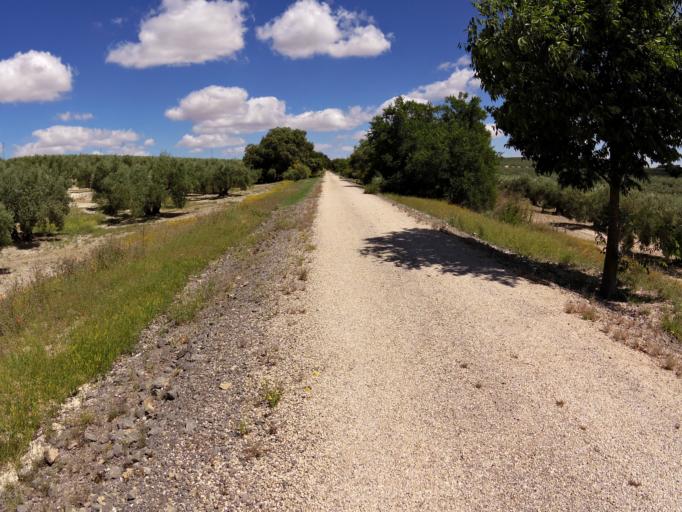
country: ES
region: Andalusia
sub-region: Provincia de Jaen
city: Alcaudete
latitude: 37.6561
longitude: -4.0621
